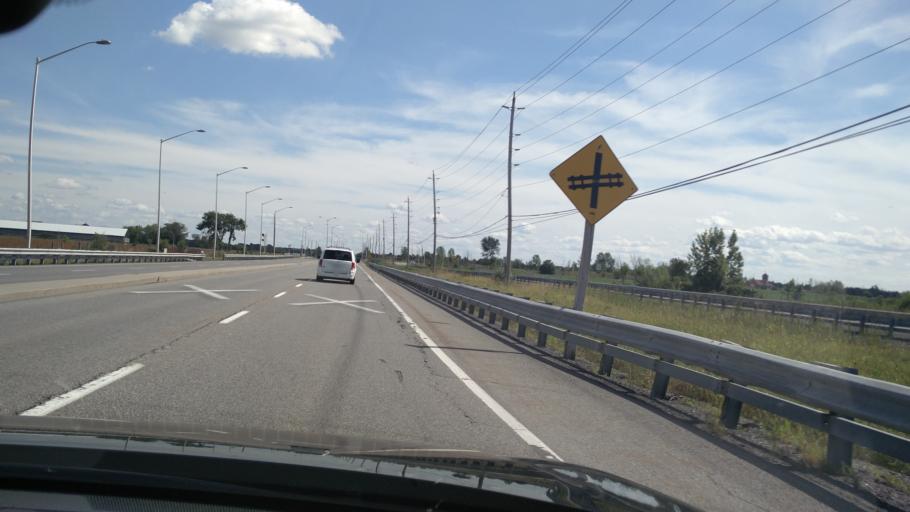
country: CA
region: Ontario
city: Bells Corners
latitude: 45.3061
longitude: -75.7356
